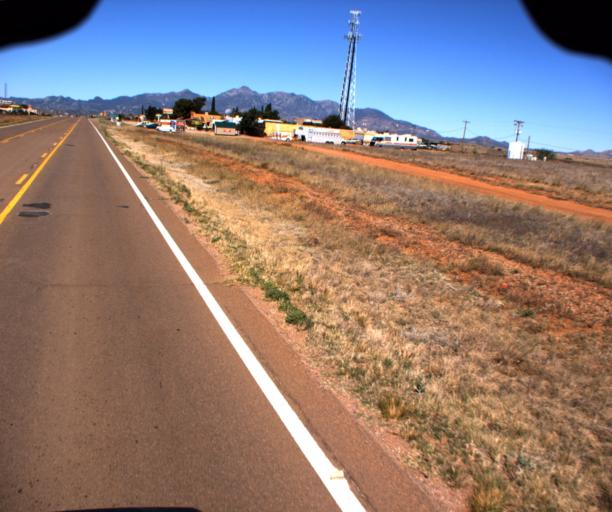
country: US
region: Arizona
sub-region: Pima County
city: Corona de Tucson
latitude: 31.6800
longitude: -110.6506
